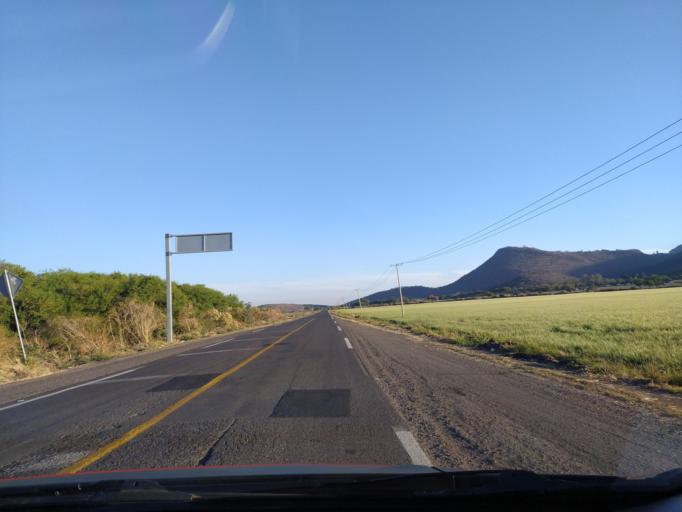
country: MX
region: Guanajuato
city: Ciudad Manuel Doblado
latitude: 20.7807
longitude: -101.8334
